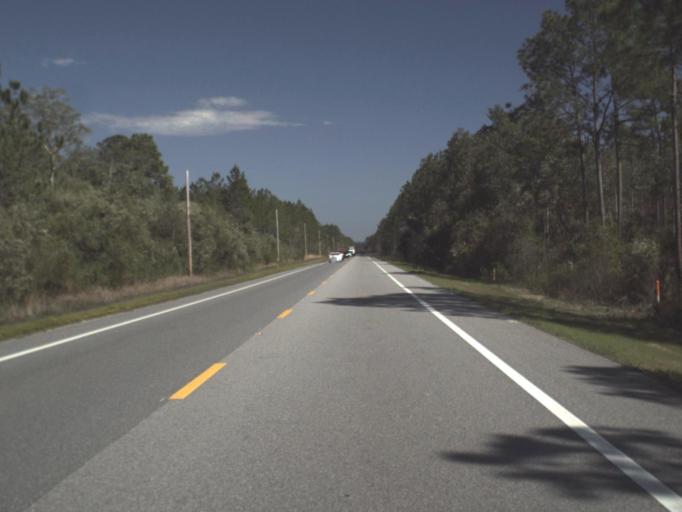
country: US
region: Florida
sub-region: Bay County
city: Lynn Haven
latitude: 30.3269
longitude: -85.7084
